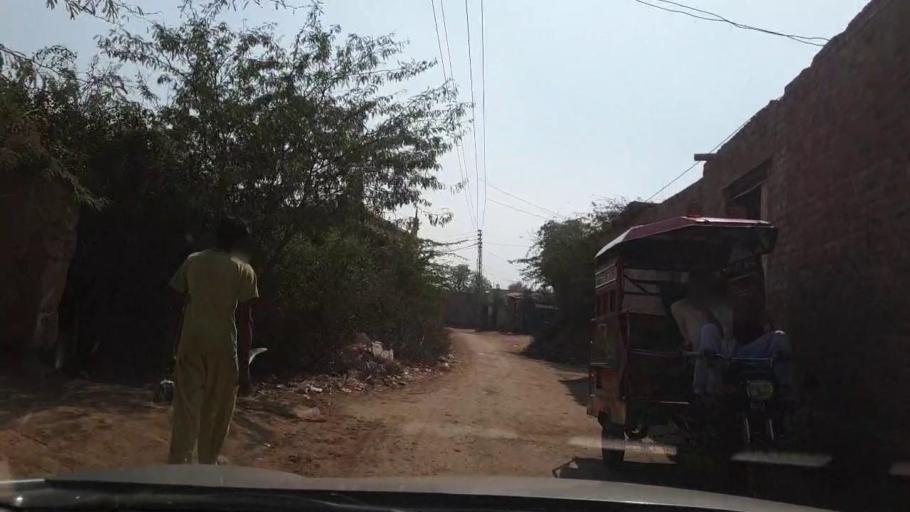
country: PK
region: Sindh
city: Tando Allahyar
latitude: 25.5037
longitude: 68.7917
